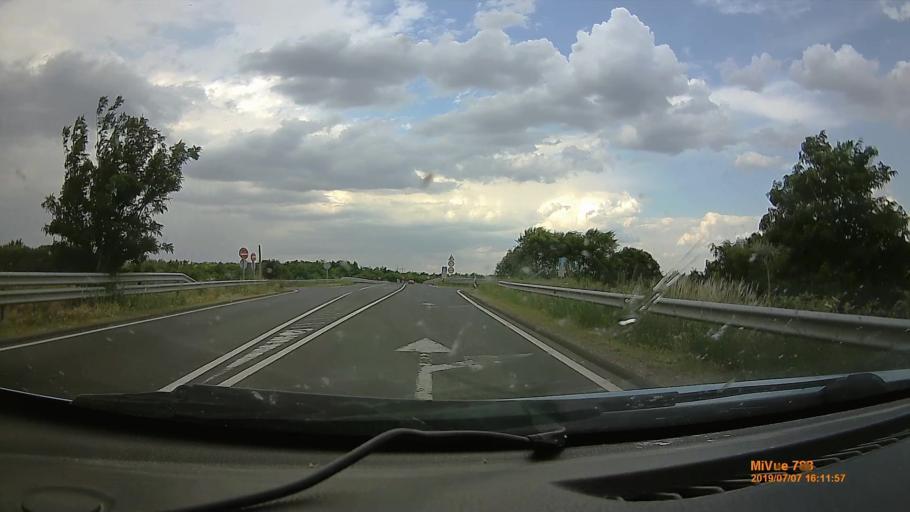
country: HU
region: Heves
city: Hatvan
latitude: 47.6825
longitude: 19.7157
